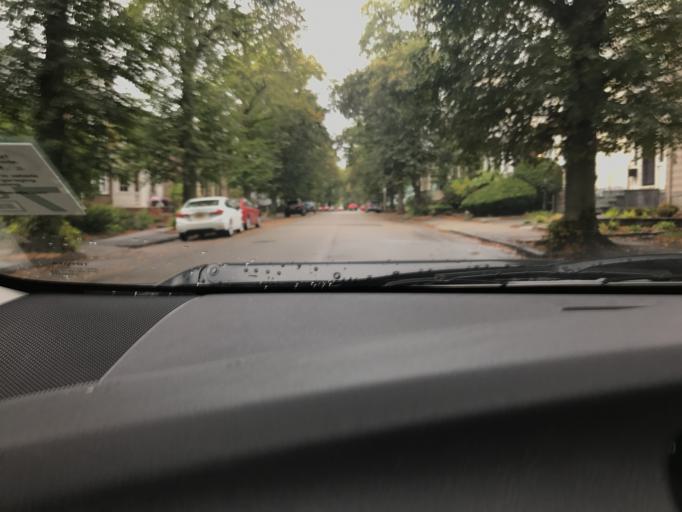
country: US
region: Massachusetts
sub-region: Suffolk County
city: Jamaica Plain
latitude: 42.3199
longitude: -71.1142
